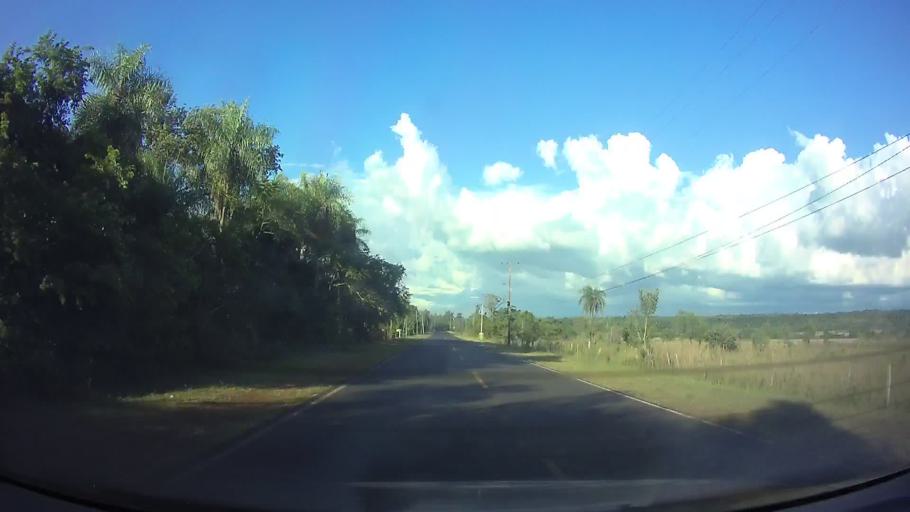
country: PY
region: Cordillera
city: Emboscada
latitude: -25.1631
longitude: -57.2673
